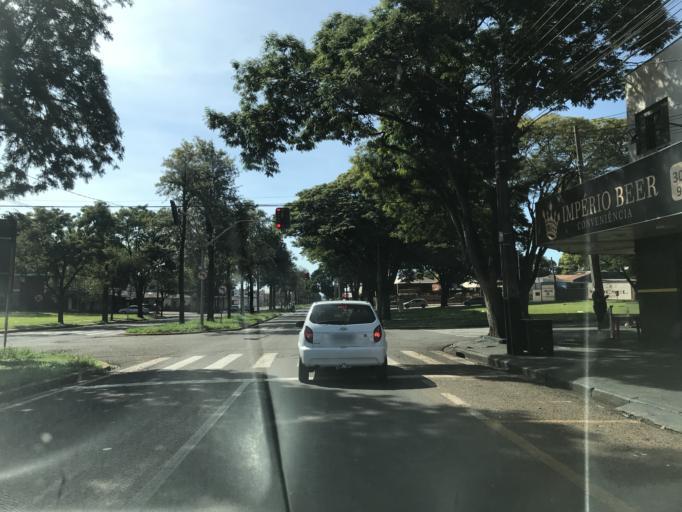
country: BR
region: Parana
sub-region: Maringa
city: Maringa
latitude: -23.3946
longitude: -51.9241
